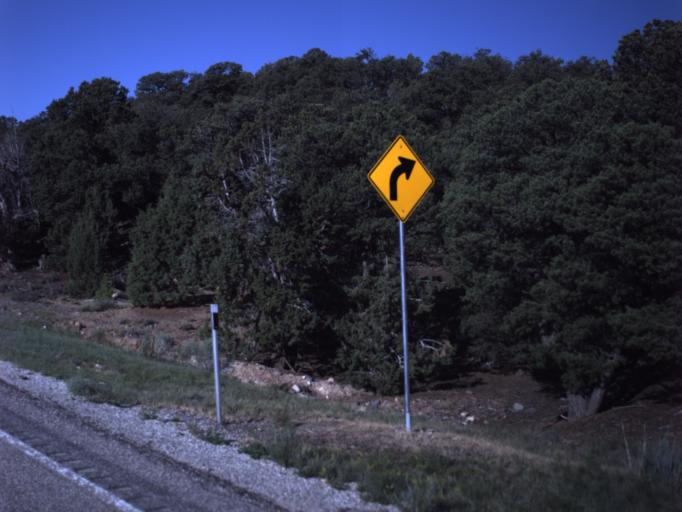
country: US
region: Utah
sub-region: Wayne County
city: Loa
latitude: 38.7175
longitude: -111.3989
